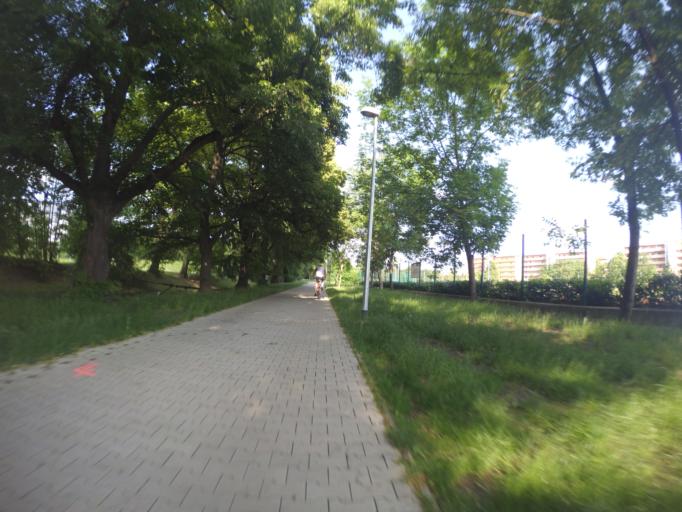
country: CZ
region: Praha
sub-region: Praha 8
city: Liben
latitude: 50.1097
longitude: 14.4890
